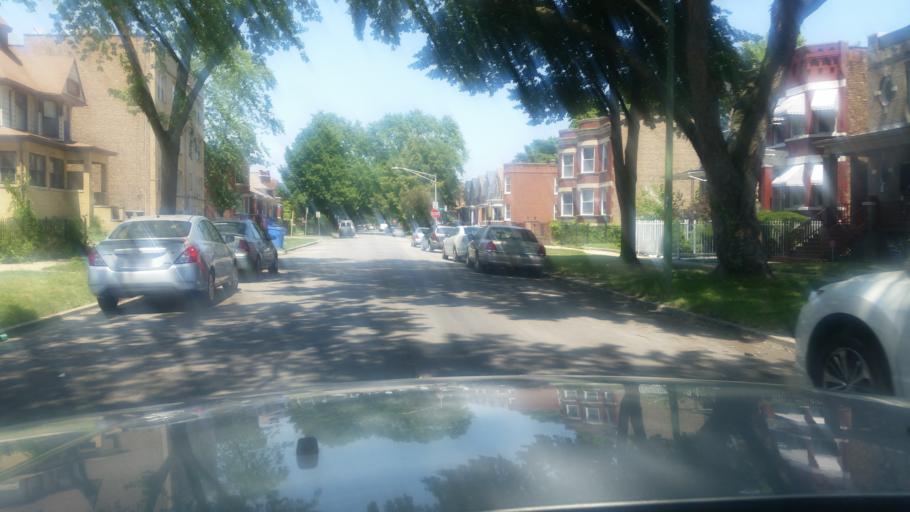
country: US
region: Illinois
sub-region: Cook County
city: Chicago
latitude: 41.7668
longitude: -87.6185
